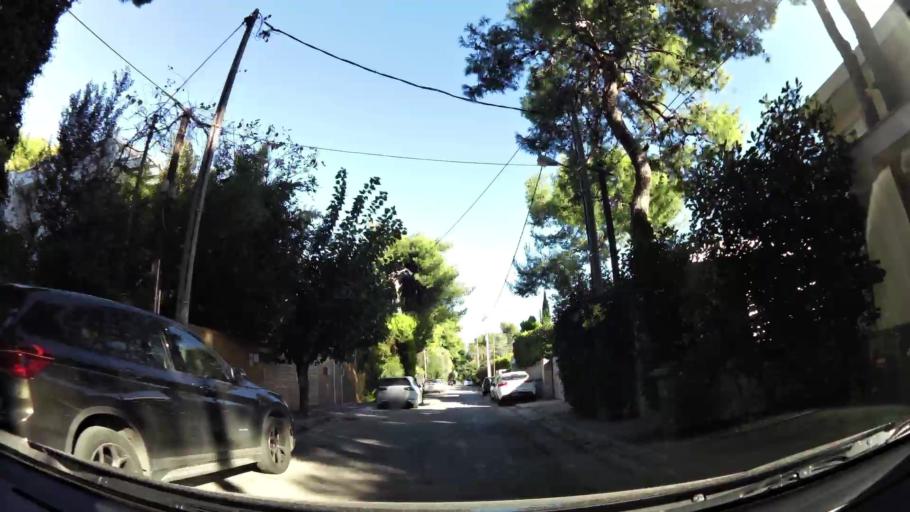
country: GR
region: Attica
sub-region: Nomarchia Athinas
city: Ekali
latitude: 38.1126
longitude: 23.8497
